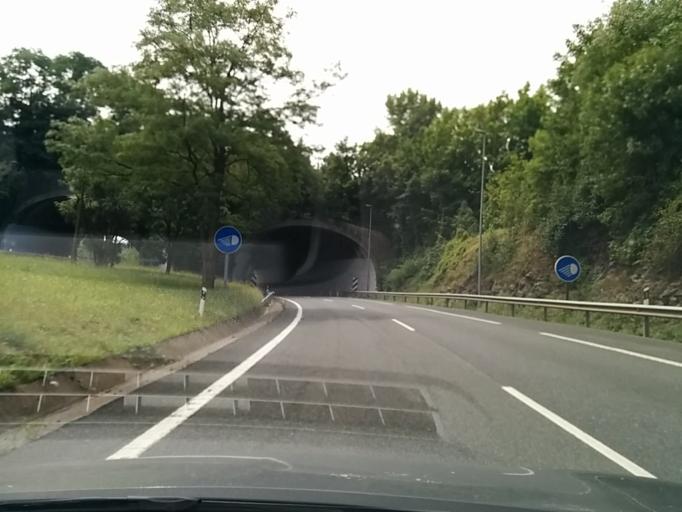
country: ES
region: Basque Country
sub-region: Provincia de Guipuzcoa
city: San Sebastian
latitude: 43.3041
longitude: -1.9698
